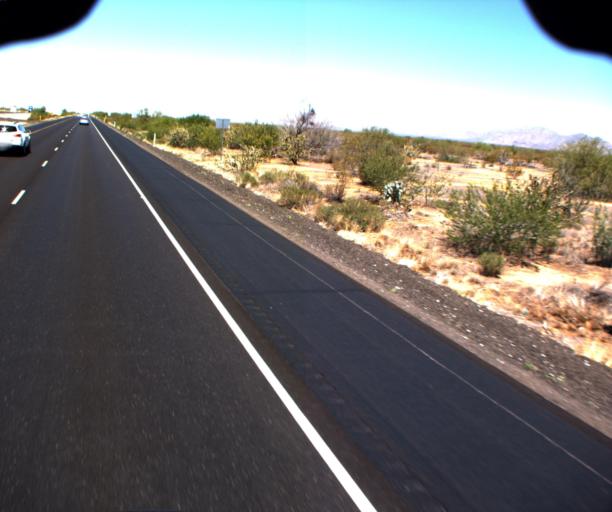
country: US
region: Arizona
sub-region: Yavapai County
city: Congress
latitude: 34.0803
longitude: -112.8886
